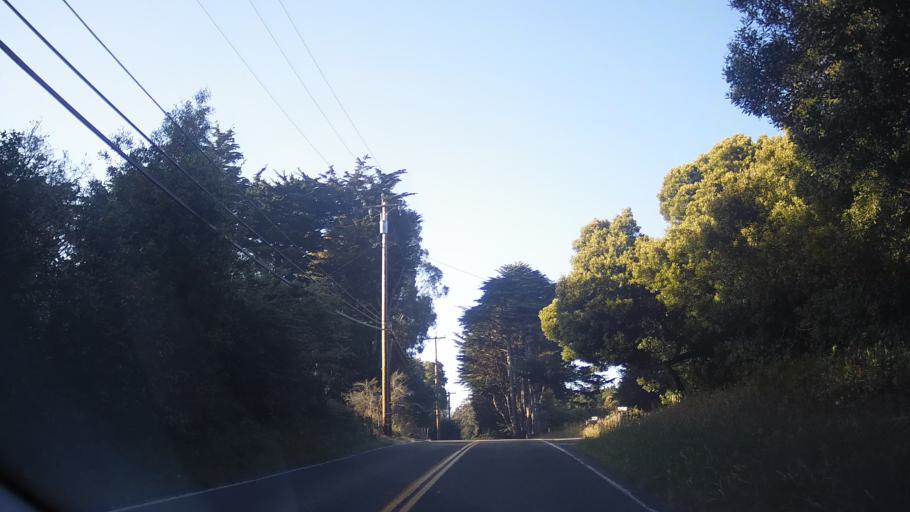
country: US
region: California
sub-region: Mendocino County
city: Fort Bragg
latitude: 39.5189
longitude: -123.7622
